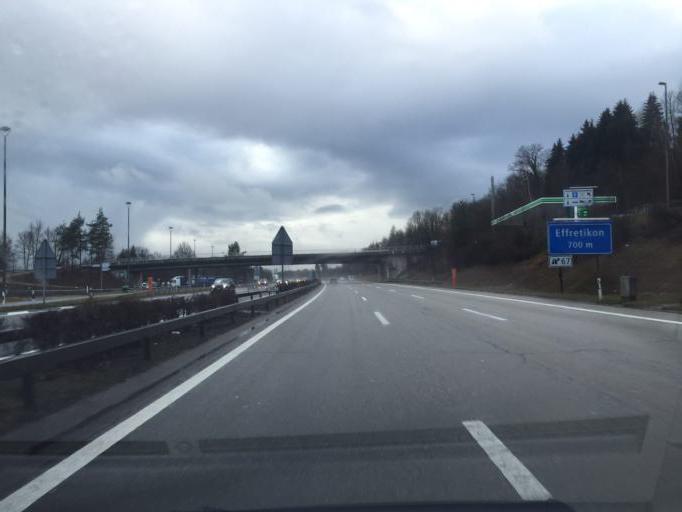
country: CH
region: Zurich
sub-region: Bezirk Pfaeffikon
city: Effretikon / Watt
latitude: 47.4525
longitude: 8.7027
